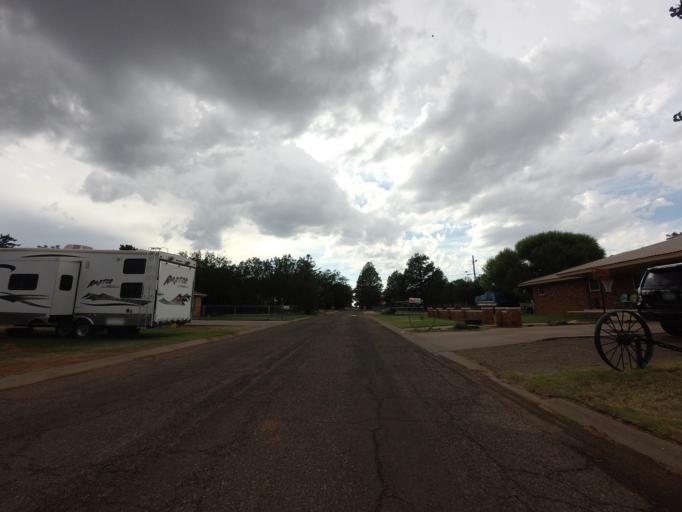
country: US
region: New Mexico
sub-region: Curry County
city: Clovis
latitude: 34.3801
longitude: -103.1996
